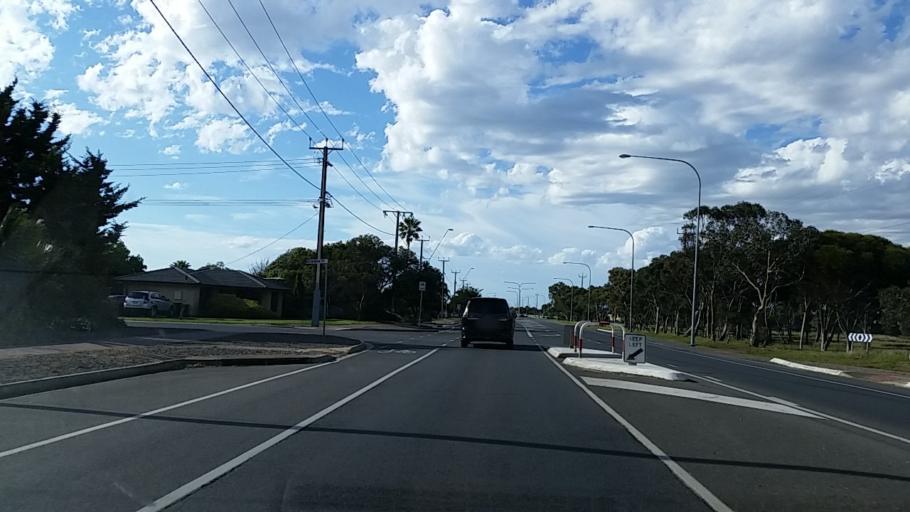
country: AU
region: South Australia
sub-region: Onkaparinga
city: Seaford
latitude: -35.1843
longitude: 138.4770
